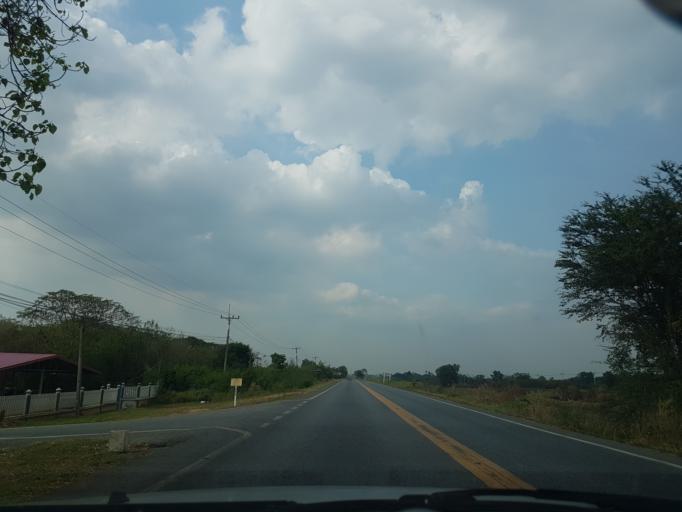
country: TH
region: Phra Nakhon Si Ayutthaya
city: Phachi
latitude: 14.4704
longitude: 100.7482
